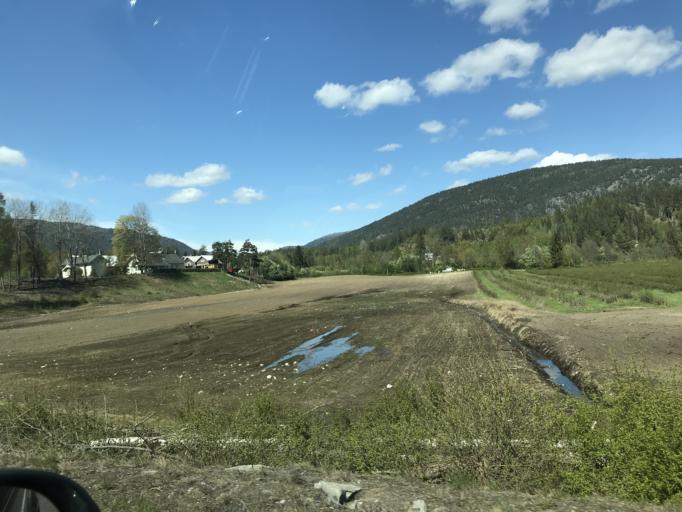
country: NO
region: Telemark
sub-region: Hjartdal
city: Sauland
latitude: 59.6088
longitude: 8.9745
